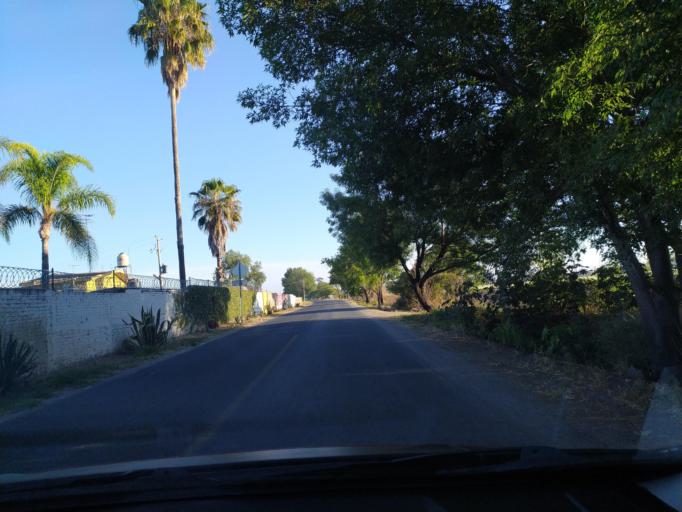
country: MX
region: Guanajuato
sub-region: San Francisco del Rincon
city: San Ignacio de Hidalgo
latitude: 20.8840
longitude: -101.8580
